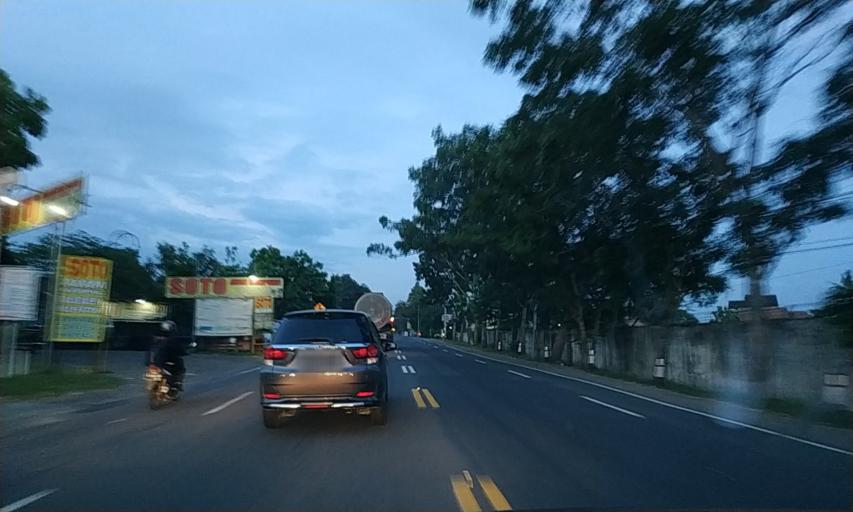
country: ID
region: Daerah Istimewa Yogyakarta
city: Godean
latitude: -7.8262
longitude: 110.2261
